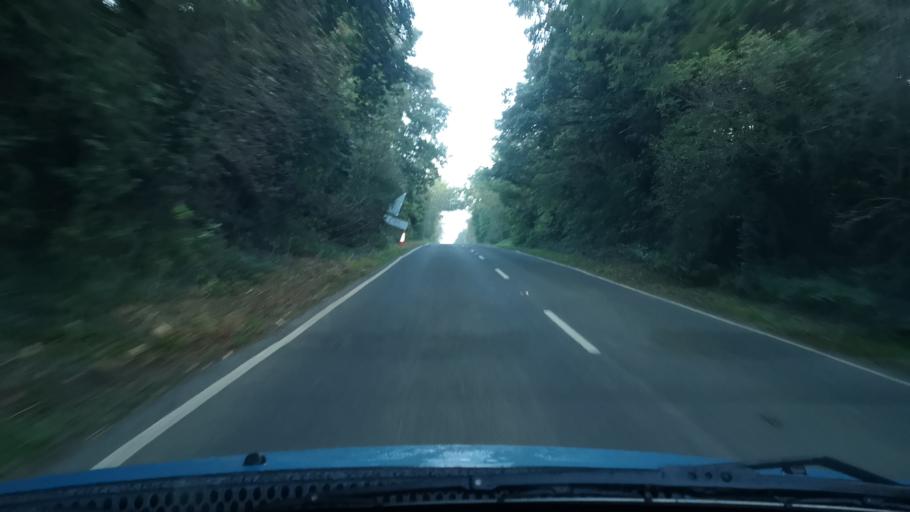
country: GB
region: England
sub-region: City and Borough of Wakefield
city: Darrington
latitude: 53.6552
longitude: -1.2659
